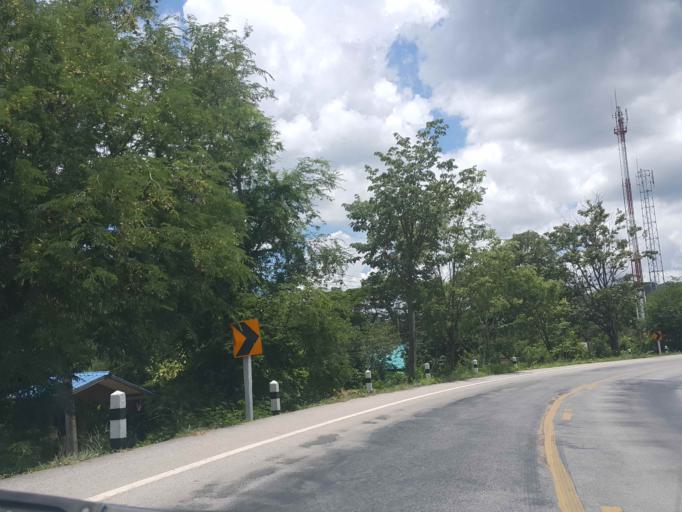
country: TH
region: Nan
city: Wiang Sa
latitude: 18.5212
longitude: 100.5594
